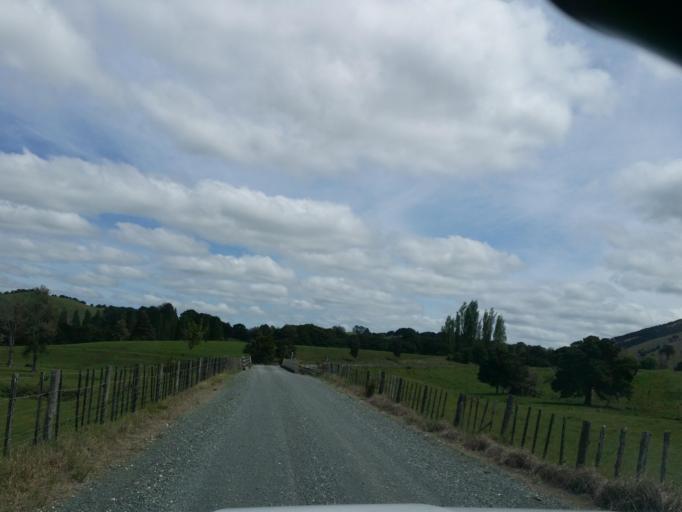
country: NZ
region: Northland
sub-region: Whangarei
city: Maungatapere
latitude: -35.9113
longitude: 174.1332
